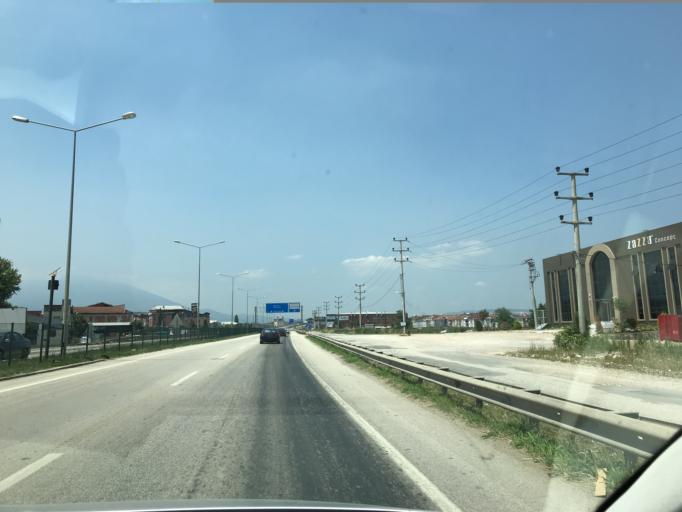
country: TR
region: Bursa
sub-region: Inegoel
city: Inegol
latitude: 40.0751
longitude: 29.5337
